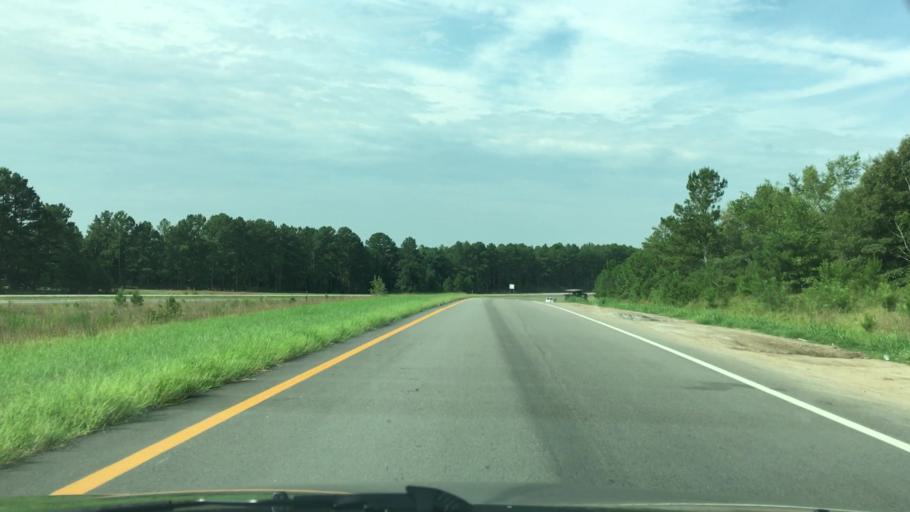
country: US
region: South Carolina
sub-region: Lexington County
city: Batesburg
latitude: 33.7526
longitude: -81.5292
